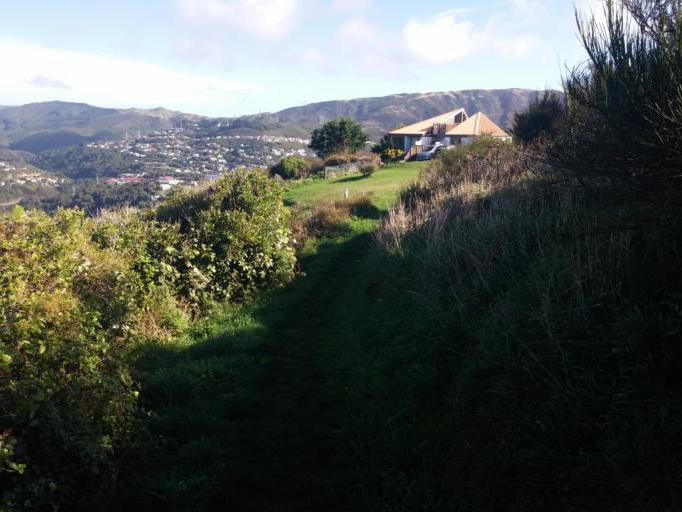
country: NZ
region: Wellington
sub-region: Wellington City
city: Kelburn
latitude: -41.2539
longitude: 174.7823
